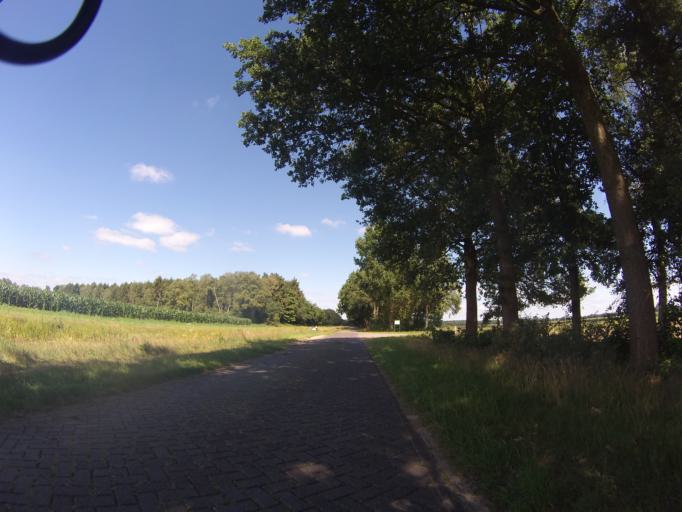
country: NL
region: Drenthe
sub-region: Gemeente Coevorden
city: Dalen
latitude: 52.7470
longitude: 6.7609
